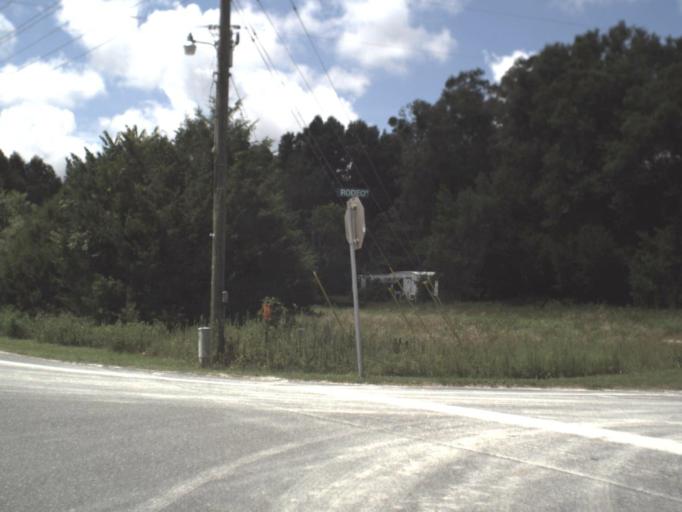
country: US
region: Florida
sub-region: Gilchrist County
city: Trenton
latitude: 29.7599
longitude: -82.8653
